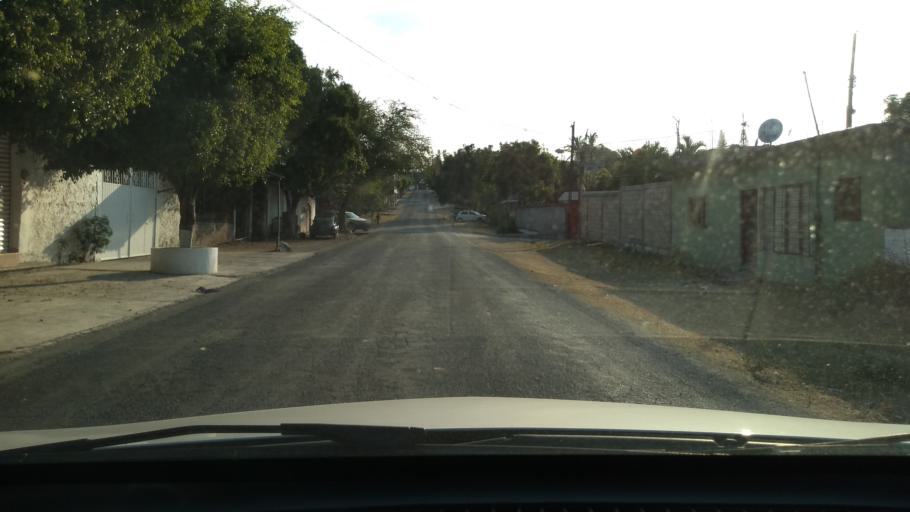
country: MX
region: Morelos
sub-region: Jojutla
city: Tehuixtla
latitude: 18.5636
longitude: -99.2717
